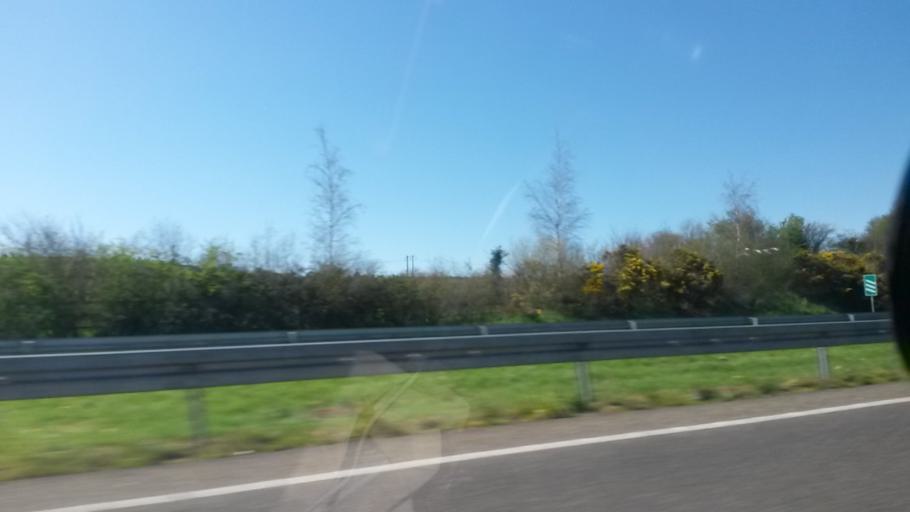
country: IE
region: Munster
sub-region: County Cork
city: Tower
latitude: 51.8744
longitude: -8.6046
